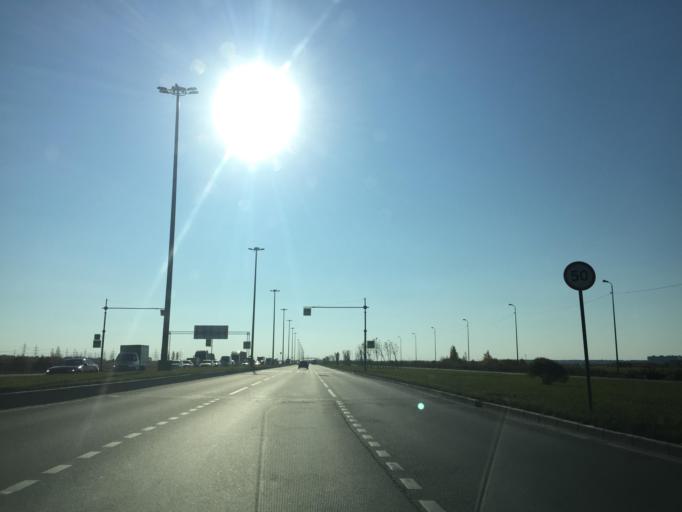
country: RU
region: St.-Petersburg
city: Petro-Slavyanka
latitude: 59.7791
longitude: 30.4977
